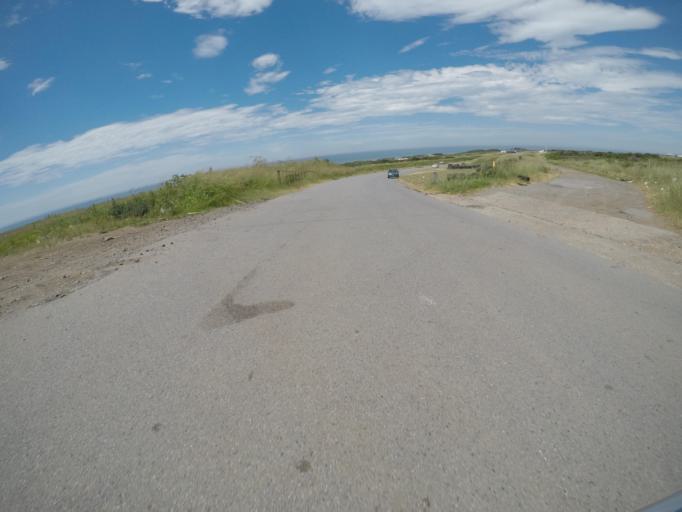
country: ZA
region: Eastern Cape
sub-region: Buffalo City Metropolitan Municipality
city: East London
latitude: -33.0432
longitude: 27.8727
